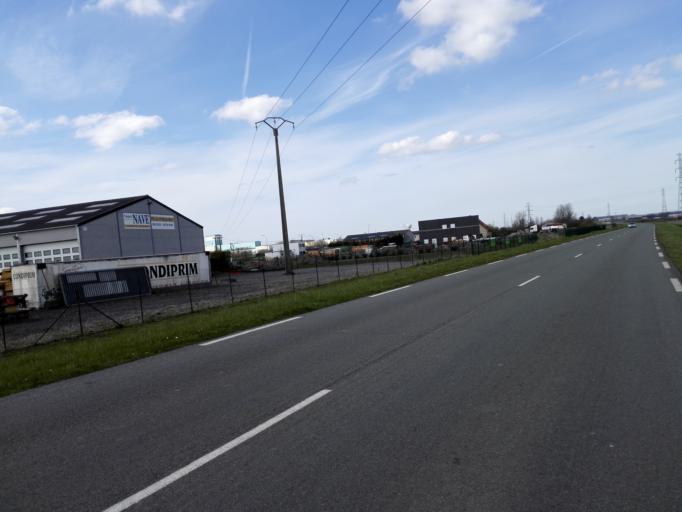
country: FR
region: Nord-Pas-de-Calais
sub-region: Departement du Nord
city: Spycker
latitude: 50.9804
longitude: 2.3065
